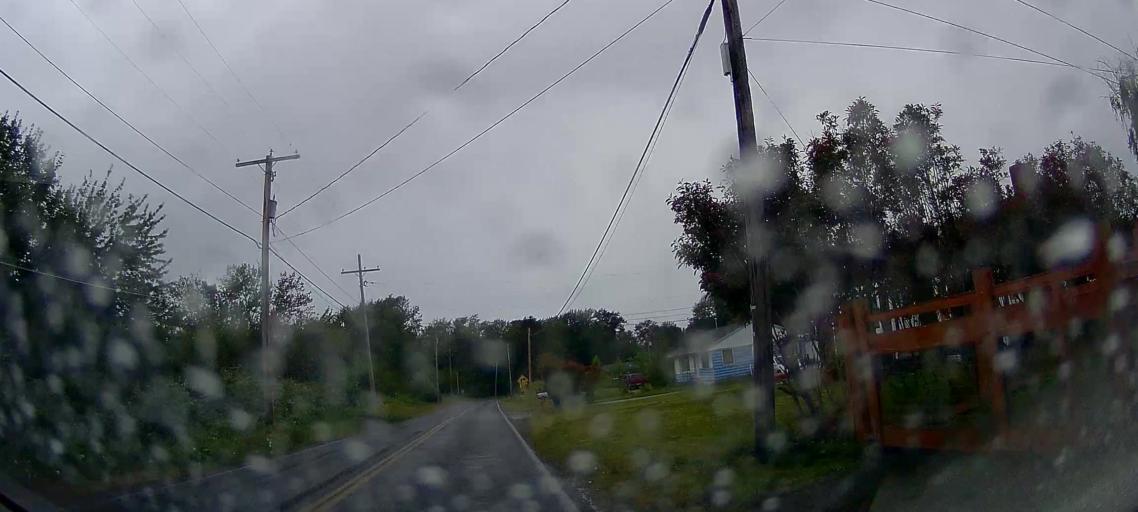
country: US
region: Washington
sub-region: Whatcom County
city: Marietta
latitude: 48.7830
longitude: -122.5719
